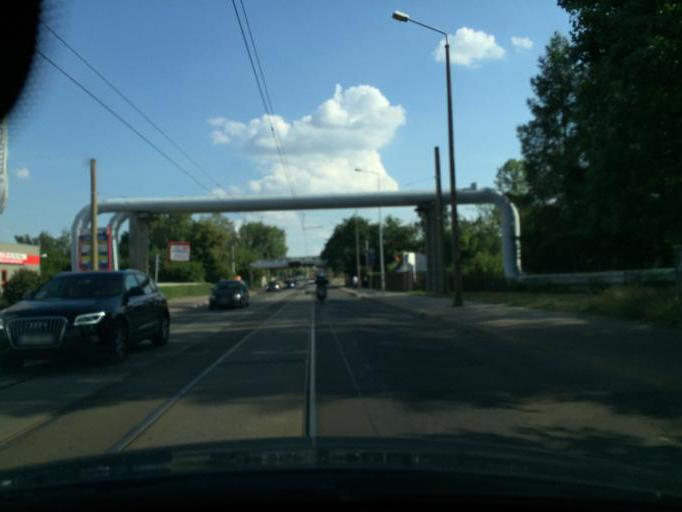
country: DE
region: Saxony
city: Leipzig
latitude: 51.3096
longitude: 12.3262
